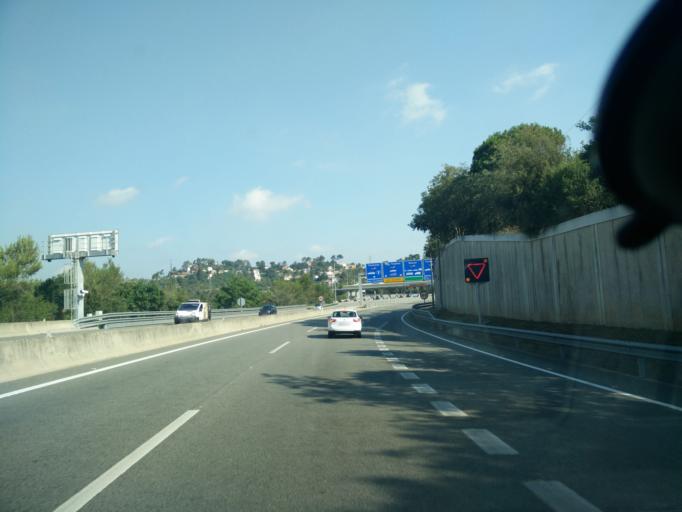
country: ES
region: Catalonia
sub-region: Provincia de Barcelona
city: Sant Cugat del Valles
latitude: 41.4347
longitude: 2.0762
